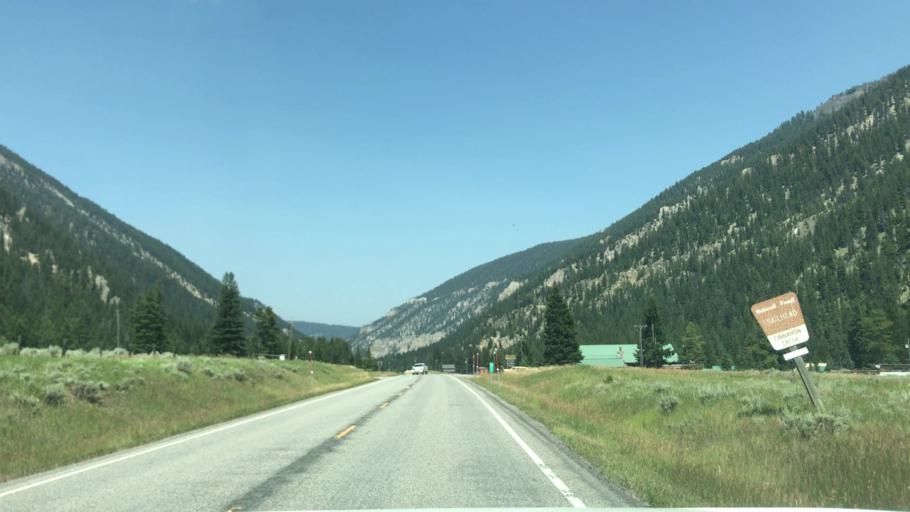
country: US
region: Montana
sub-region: Gallatin County
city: Big Sky
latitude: 45.1143
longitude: -111.2249
